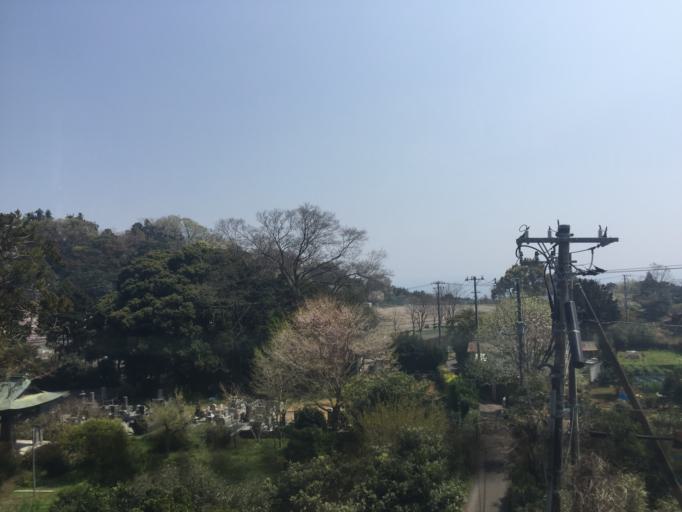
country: JP
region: Shizuoka
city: Ito
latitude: 34.9115
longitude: 139.1329
